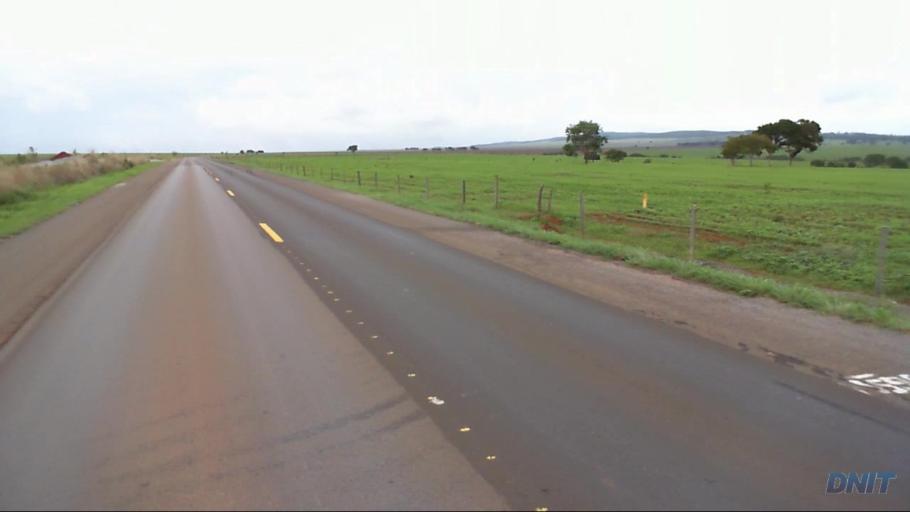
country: BR
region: Goias
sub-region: Padre Bernardo
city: Padre Bernardo
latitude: -15.1694
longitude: -48.3659
